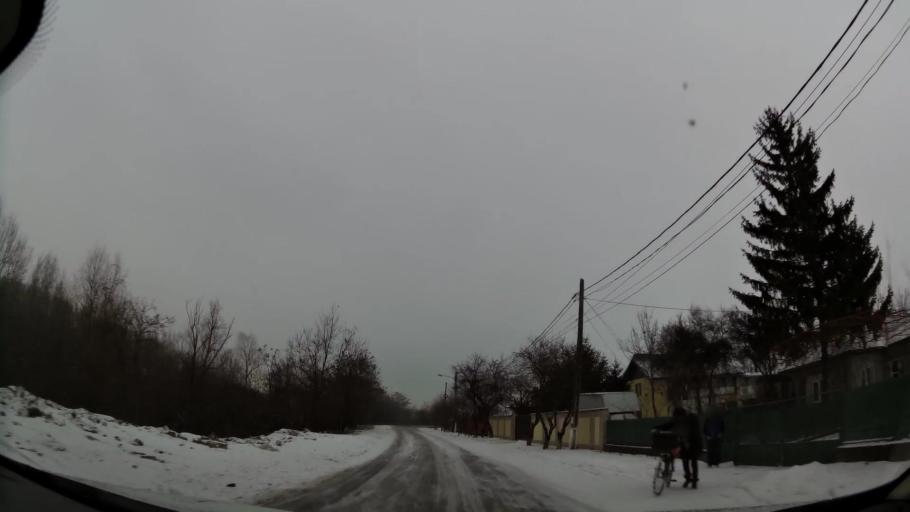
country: RO
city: Fantanele
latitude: 44.7338
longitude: 25.8985
